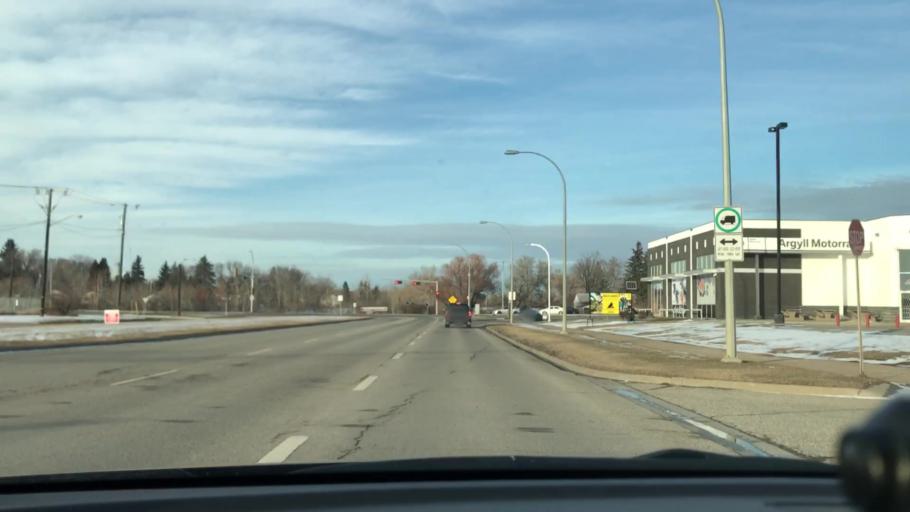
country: CA
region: Alberta
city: Edmonton
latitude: 53.4987
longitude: -113.4670
